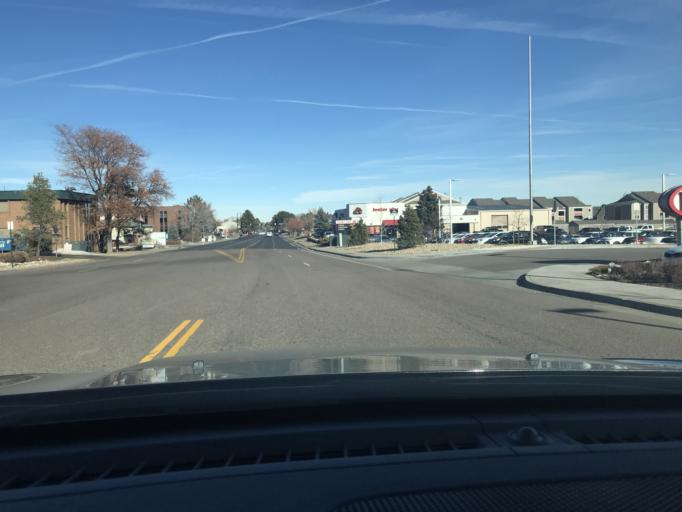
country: US
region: Colorado
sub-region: Arapahoe County
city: Centennial
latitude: 39.5957
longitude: -104.8761
